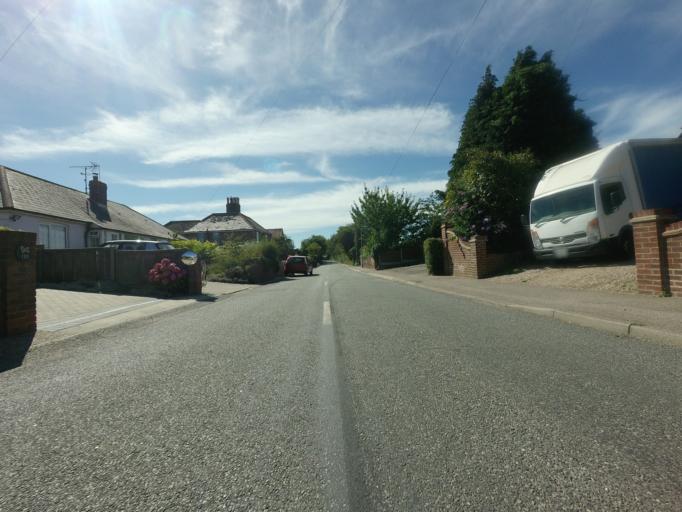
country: GB
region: England
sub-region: Kent
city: Birchington-on-Sea
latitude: 51.3358
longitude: 1.3023
